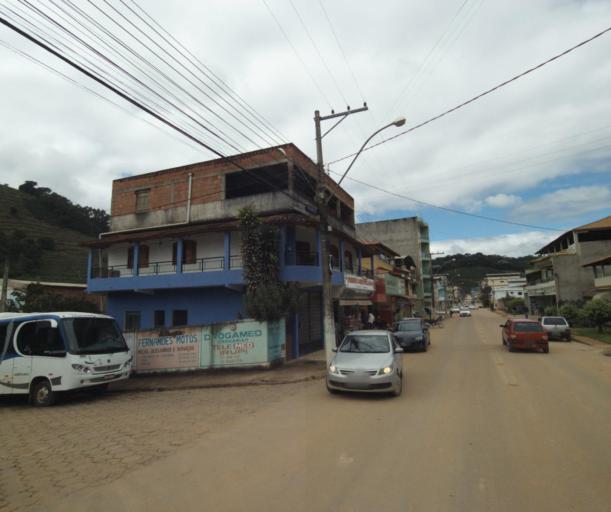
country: BR
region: Espirito Santo
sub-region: Irupi
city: Irupi
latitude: -20.3468
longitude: -41.6385
